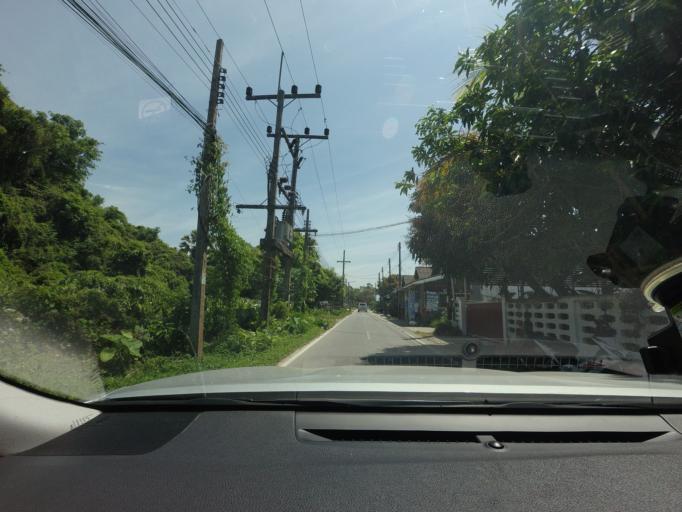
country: TH
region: Narathiwat
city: Narathiwat
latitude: 6.4444
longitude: 101.8100
